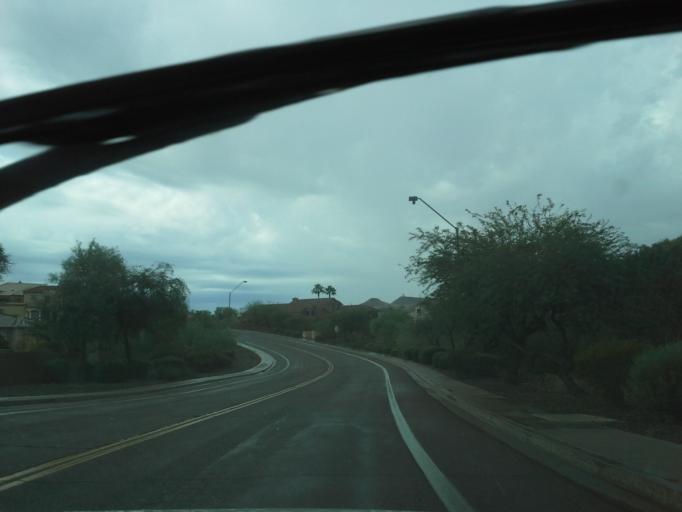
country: US
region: Arizona
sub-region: Maricopa County
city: Paradise Valley
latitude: 33.6101
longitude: -112.0529
